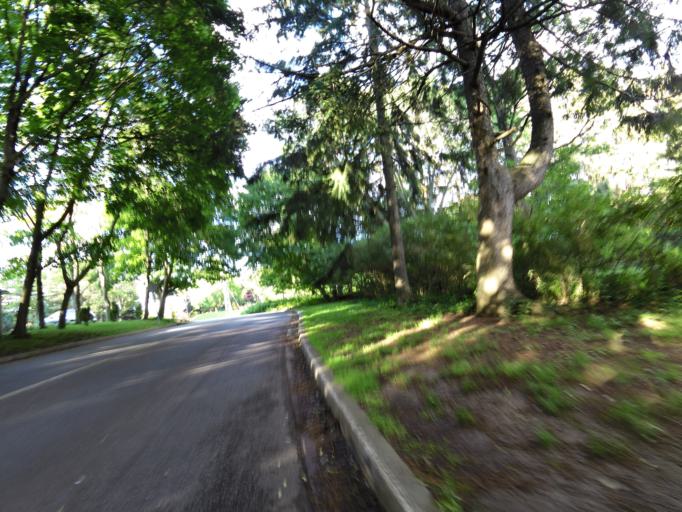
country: CA
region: Ontario
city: Scarborough
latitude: 43.7331
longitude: -79.2153
